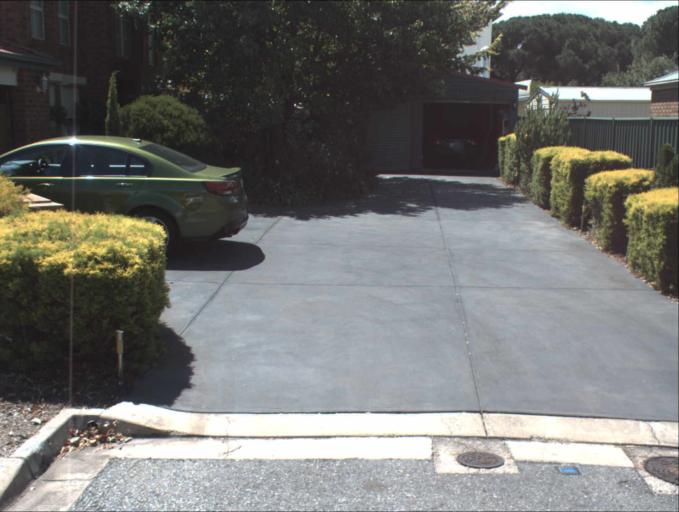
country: AU
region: South Australia
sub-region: Port Adelaide Enfield
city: Gilles Plains
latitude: -34.8538
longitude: 138.6393
